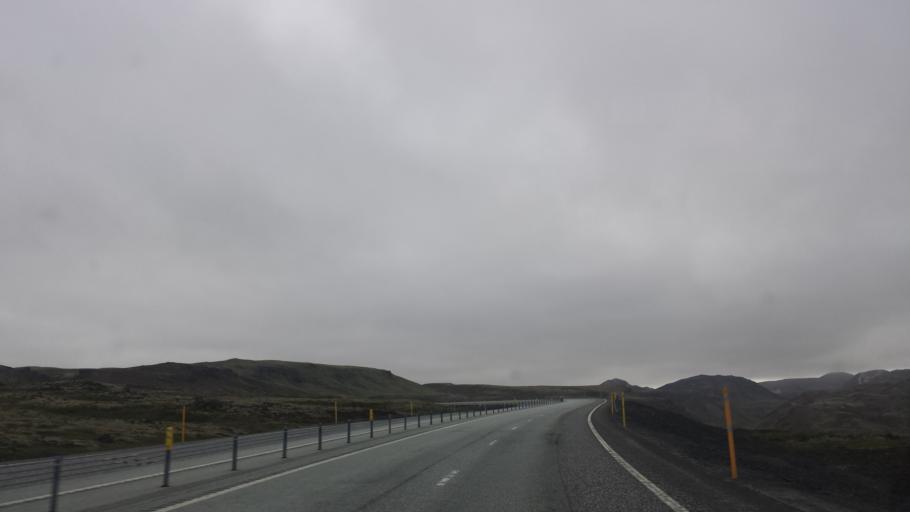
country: IS
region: South
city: Hveragerdi
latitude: 64.0108
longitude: -21.2209
